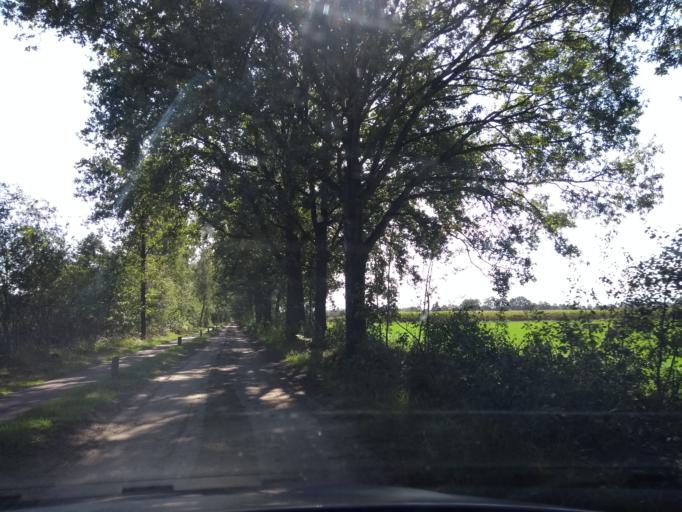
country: DE
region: Lower Saxony
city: Lage
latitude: 52.4297
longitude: 7.0019
